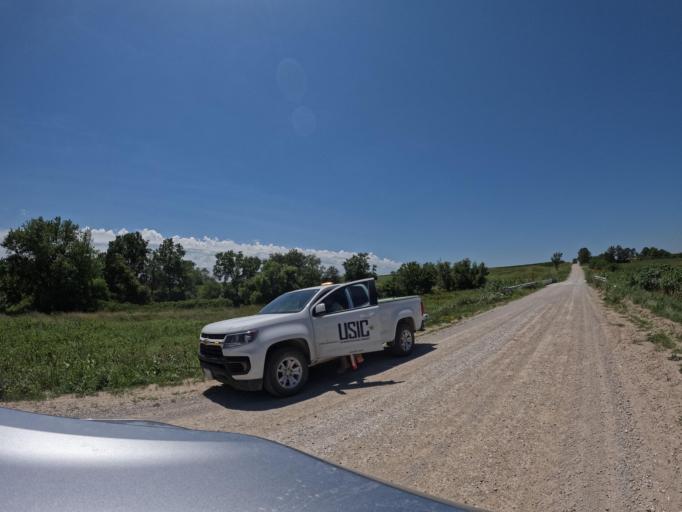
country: US
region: Iowa
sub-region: Keokuk County
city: Sigourney
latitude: 41.4089
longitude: -92.3323
